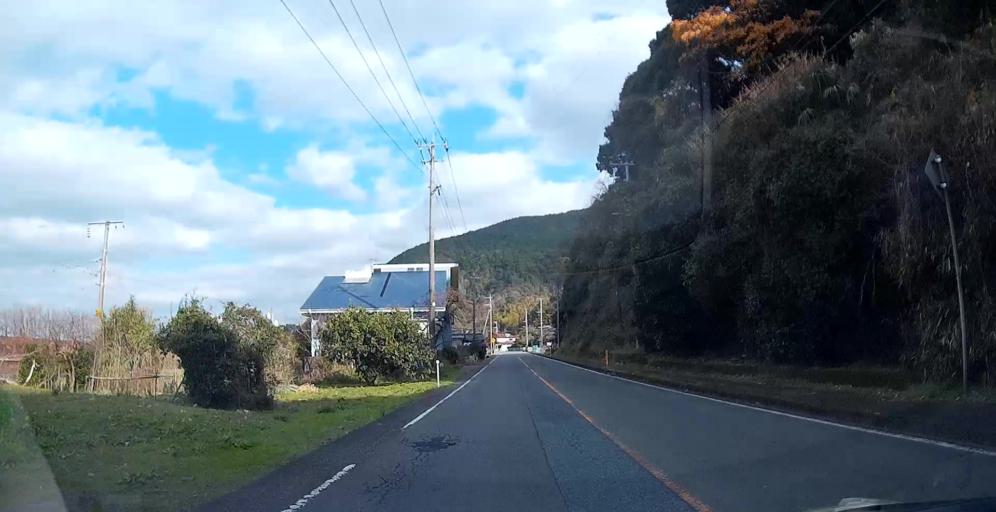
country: JP
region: Kumamoto
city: Yatsushiro
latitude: 32.4216
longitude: 130.5530
